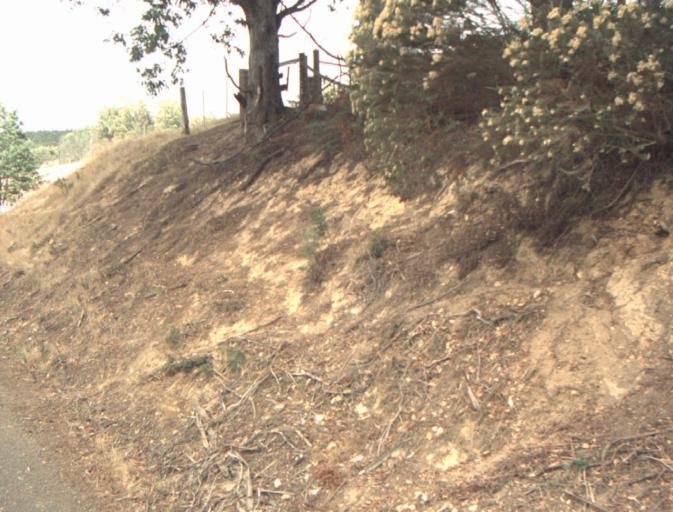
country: AU
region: Tasmania
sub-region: Dorset
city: Bridport
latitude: -41.1857
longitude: 147.2623
